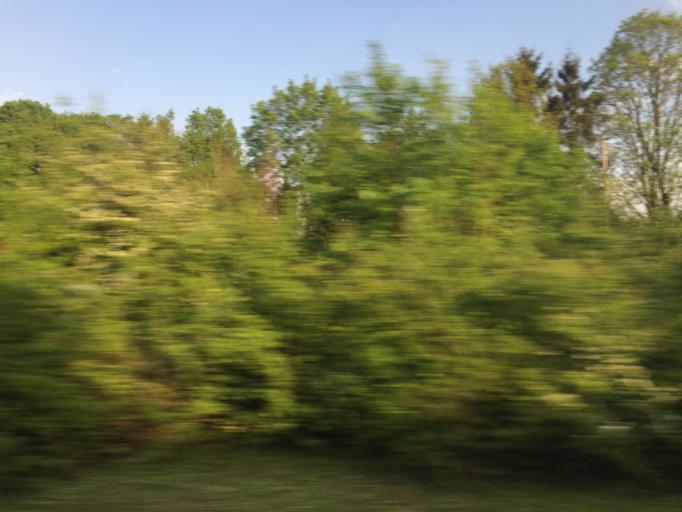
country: DE
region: North Rhine-Westphalia
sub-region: Regierungsbezirk Dusseldorf
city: Muelheim (Ruhr)
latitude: 51.4453
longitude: 6.9390
